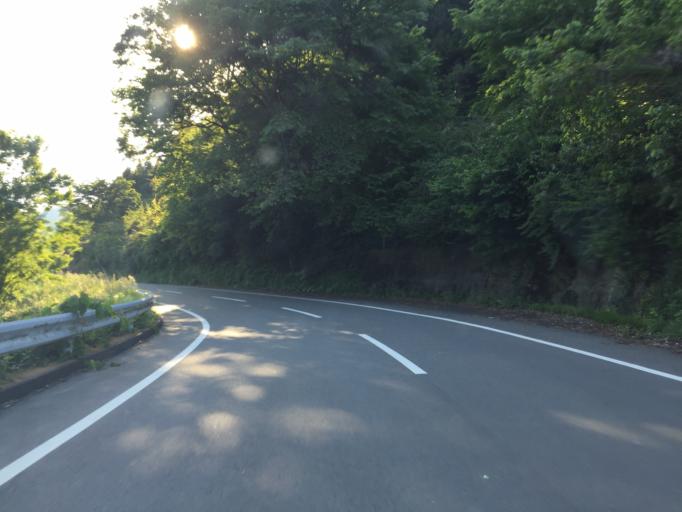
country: JP
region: Ibaraki
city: Daigo
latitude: 36.9267
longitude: 140.4571
